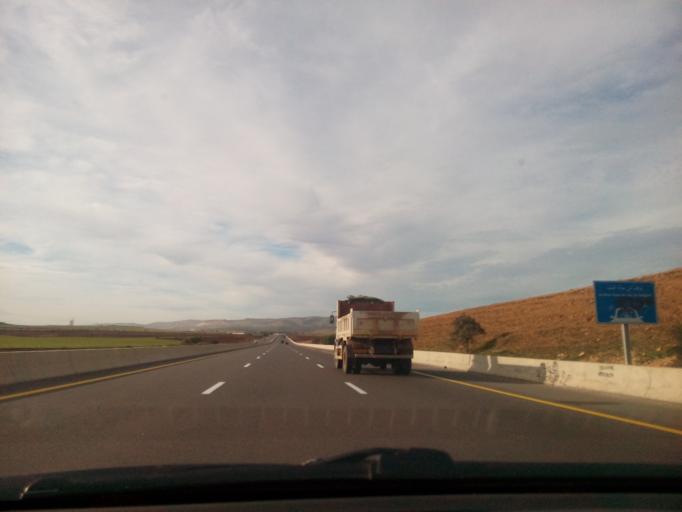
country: DZ
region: Mascara
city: Sig
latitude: 35.5074
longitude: -0.3700
